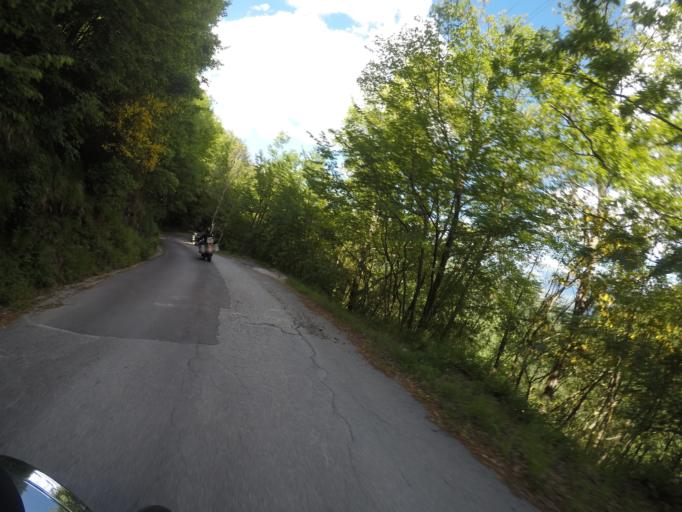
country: IT
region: Tuscany
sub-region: Provincia di Lucca
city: Minucciano
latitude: 44.1531
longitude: 10.1995
